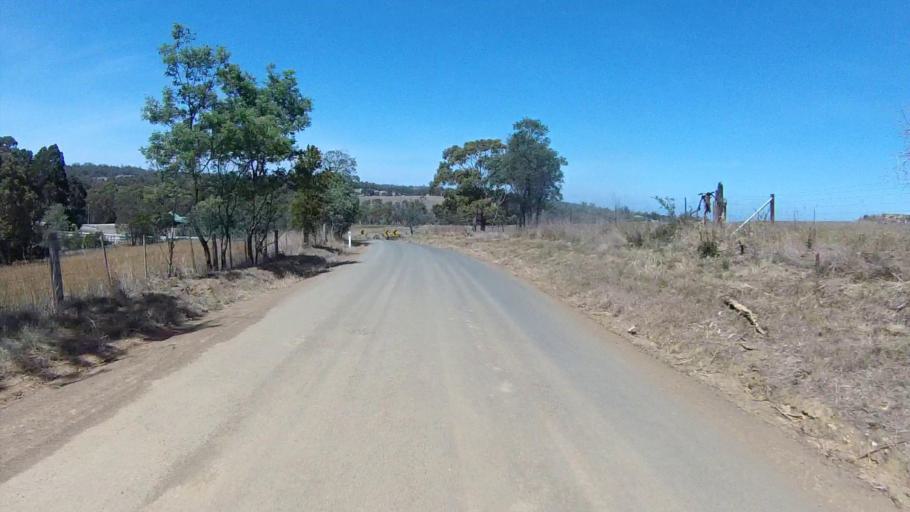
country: AU
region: Tasmania
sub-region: Sorell
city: Sorell
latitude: -42.7972
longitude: 147.6403
